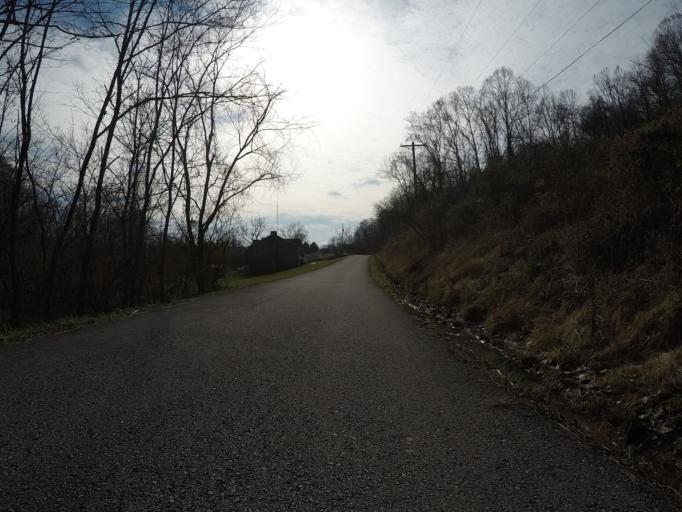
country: US
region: West Virginia
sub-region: Cabell County
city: Pea Ridge
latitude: 38.4245
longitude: -82.3413
